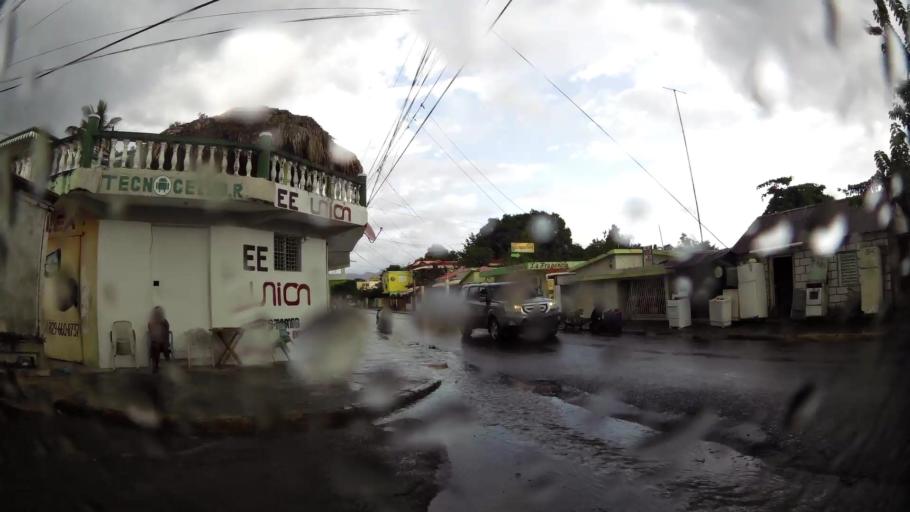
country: DO
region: Monsenor Nouel
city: Bonao
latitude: 18.9427
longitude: -70.4061
